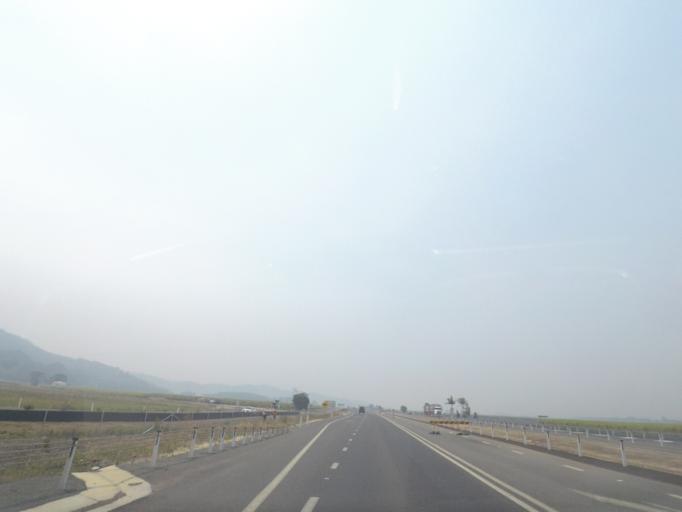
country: AU
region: New South Wales
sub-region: Ballina
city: Ballina
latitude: -28.9023
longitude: 153.4796
